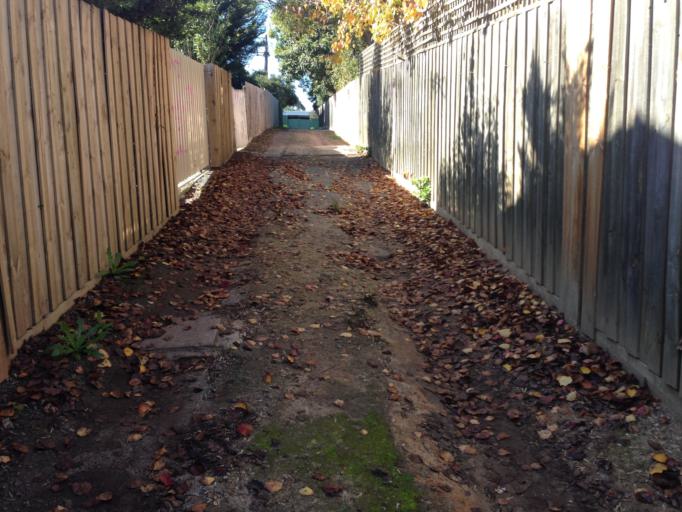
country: AU
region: Victoria
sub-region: Boroondara
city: Balwyn North
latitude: -37.7947
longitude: 145.0799
